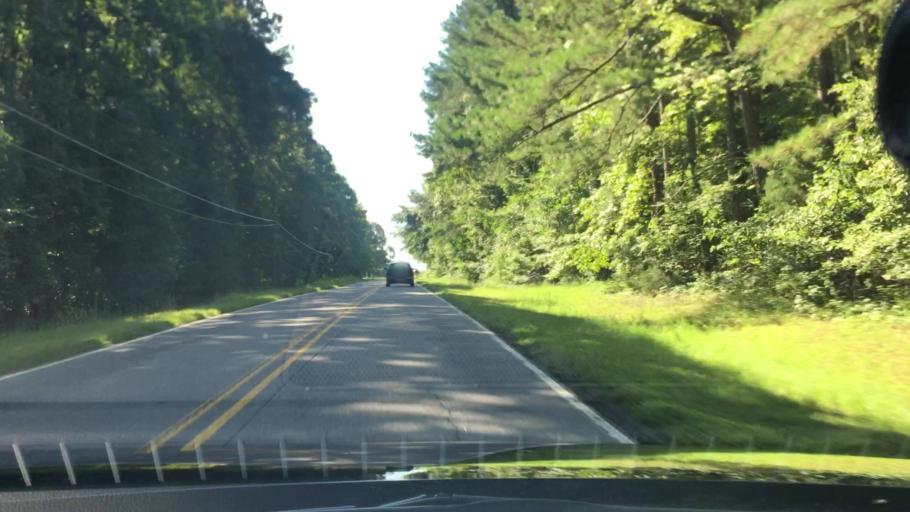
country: US
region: Georgia
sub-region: Putnam County
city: Jefferson
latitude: 33.3978
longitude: -83.2723
